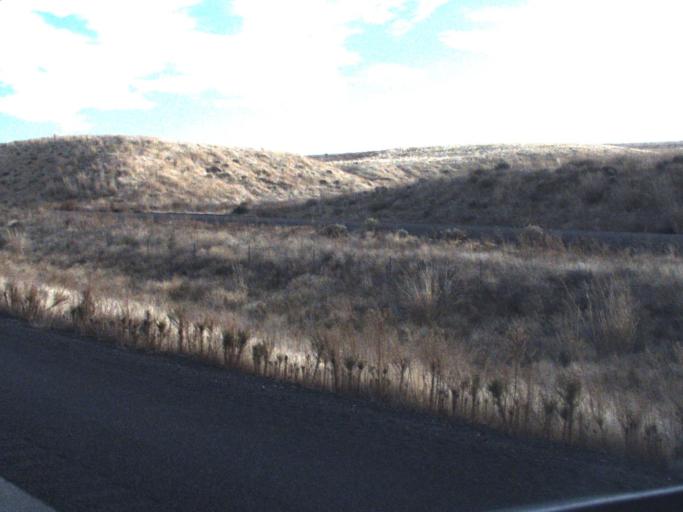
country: US
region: Washington
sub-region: Franklin County
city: Connell
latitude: 46.8446
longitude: -118.6438
